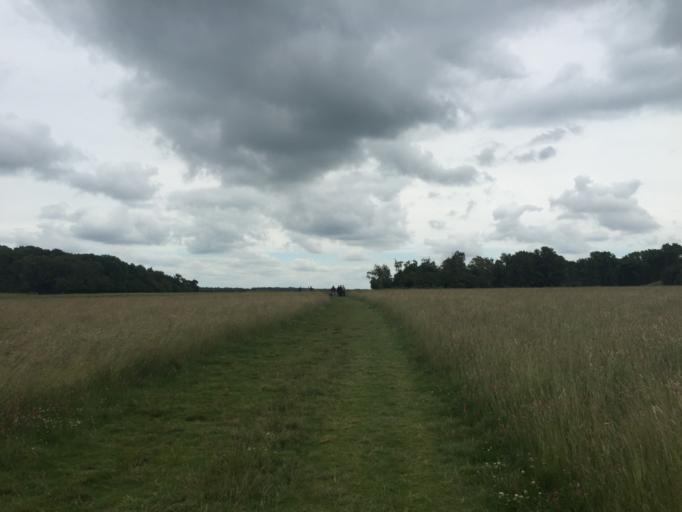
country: GB
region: England
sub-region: Wiltshire
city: Winterbourne Stoke
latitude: 51.1847
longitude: -1.8464
